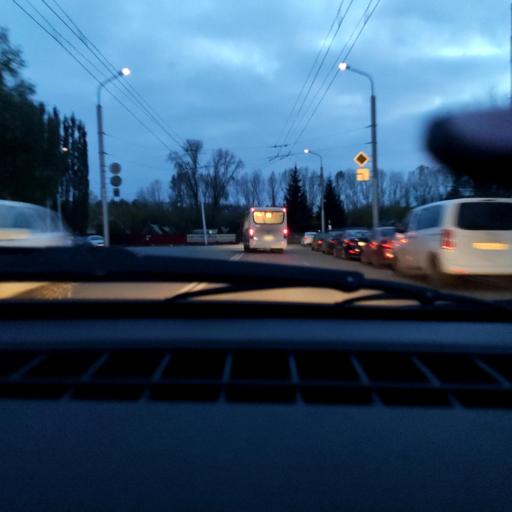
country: RU
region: Bashkortostan
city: Ufa
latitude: 54.7749
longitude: 56.1130
